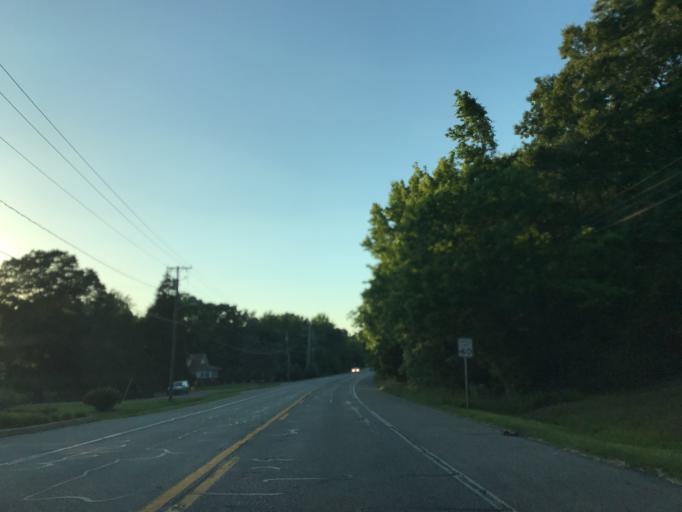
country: US
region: Maryland
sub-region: Anne Arundel County
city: Mayo
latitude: 38.8972
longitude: -76.5130
